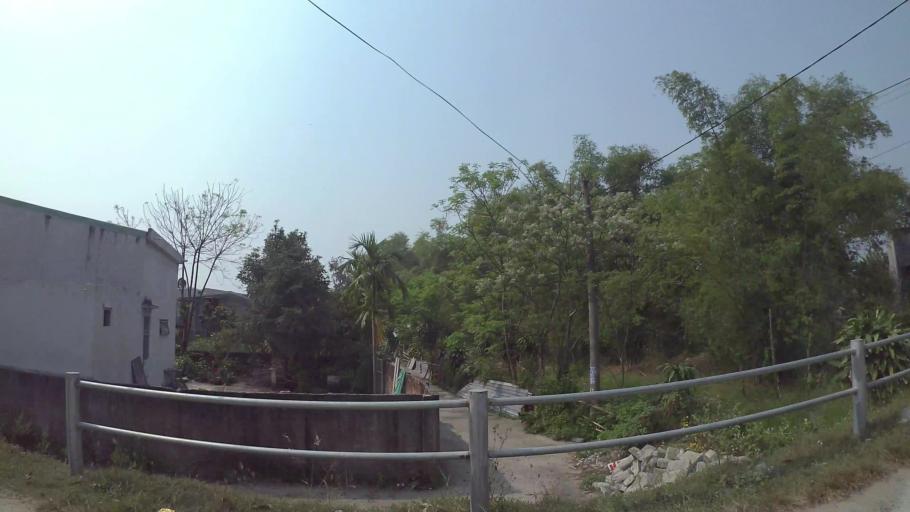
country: VN
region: Da Nang
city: Ngu Hanh Son
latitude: 15.9910
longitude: 108.2430
